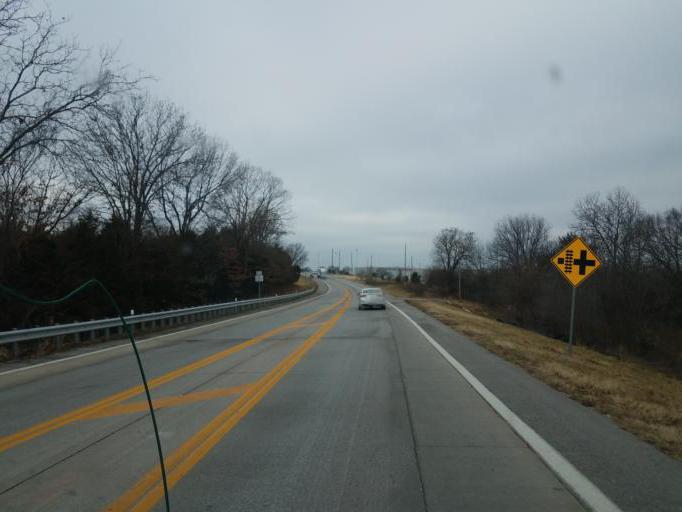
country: US
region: Missouri
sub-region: Greene County
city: Strafford
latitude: 37.2476
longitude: -93.1857
